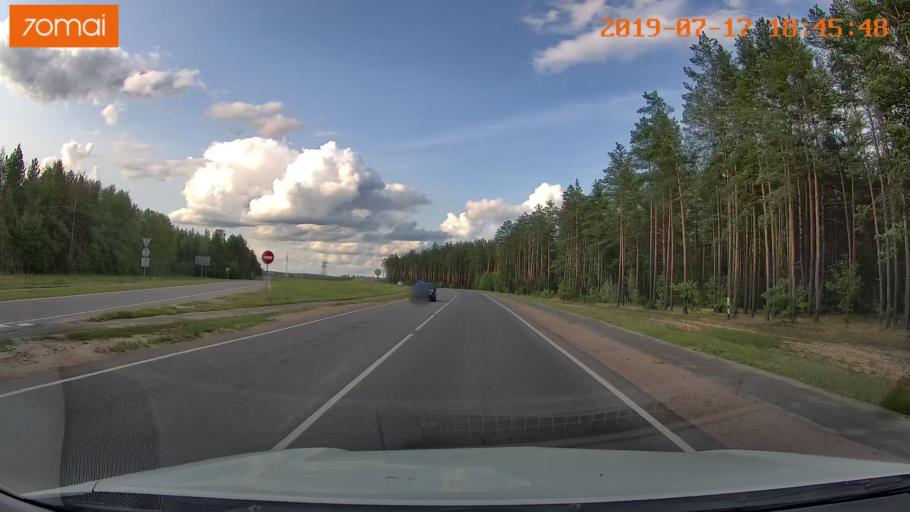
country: BY
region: Mogilev
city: Asipovichy
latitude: 53.3282
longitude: 28.6593
